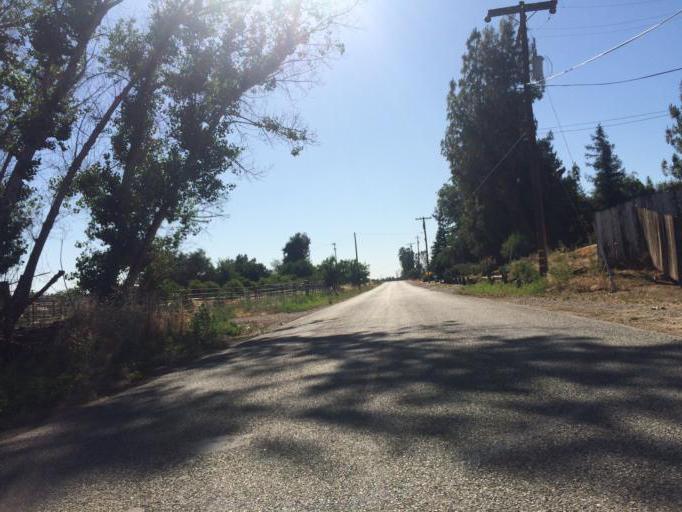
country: US
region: California
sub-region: Fresno County
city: Tarpey Village
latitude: 36.7866
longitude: -119.6146
